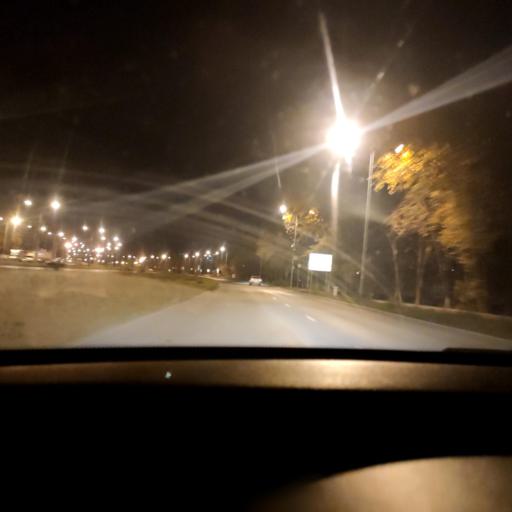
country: RU
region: Samara
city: Samara
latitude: 53.2533
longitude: 50.2474
